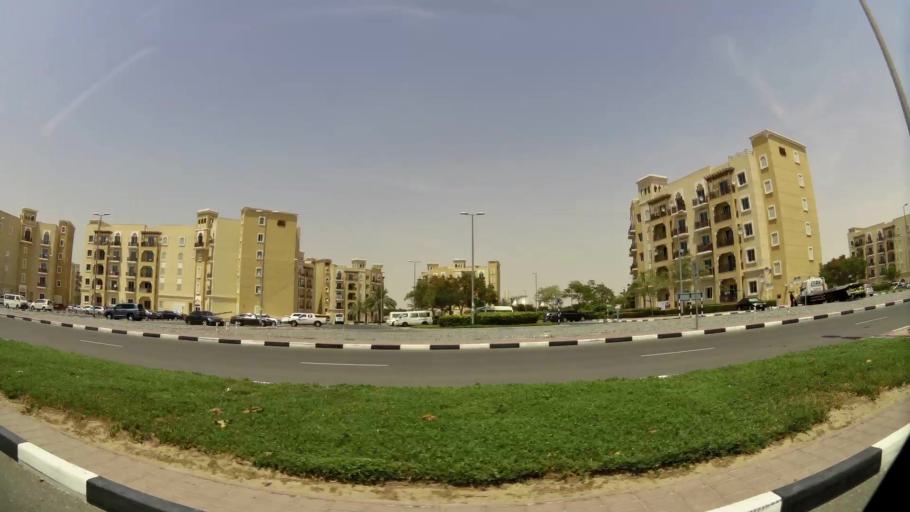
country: AE
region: Ash Shariqah
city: Sharjah
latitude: 25.1603
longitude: 55.4221
